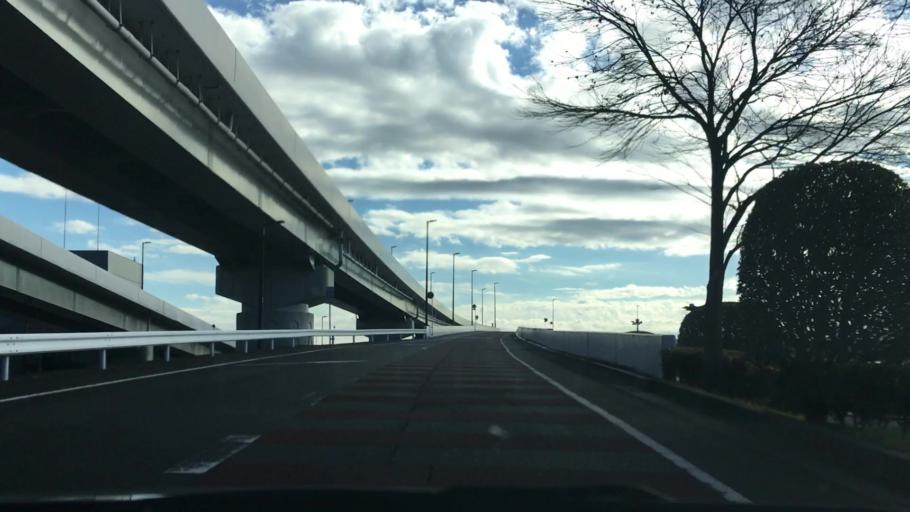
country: JP
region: Chiba
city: Narita
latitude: 35.7704
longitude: 140.3894
